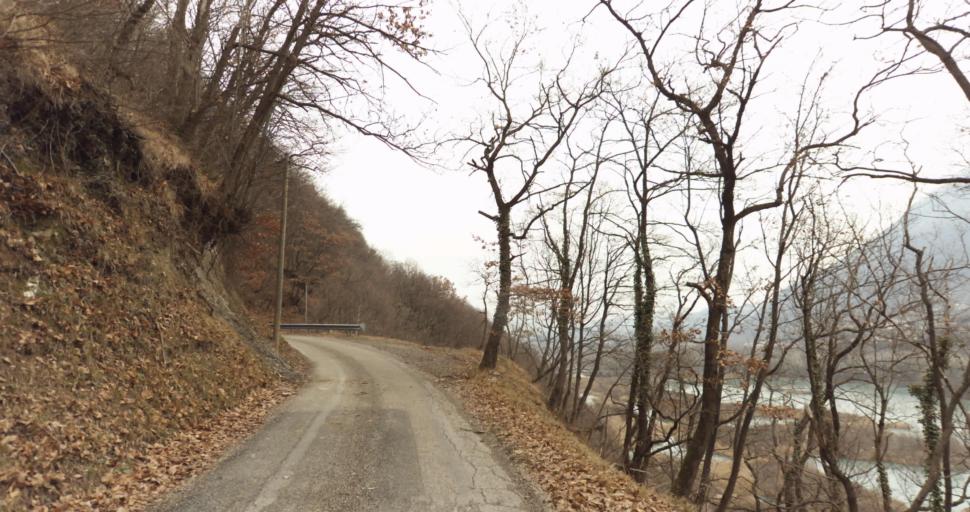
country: FR
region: Rhone-Alpes
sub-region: Departement de l'Isere
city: Saint-Georges-de-Commiers
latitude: 45.0377
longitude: 5.6910
